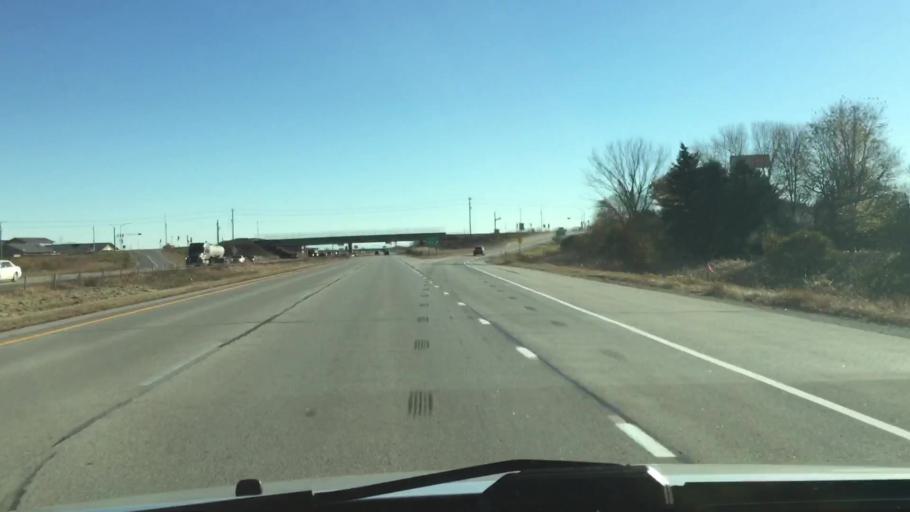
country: US
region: Wisconsin
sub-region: Outagamie County
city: Kimberly
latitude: 44.2981
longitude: -88.3795
